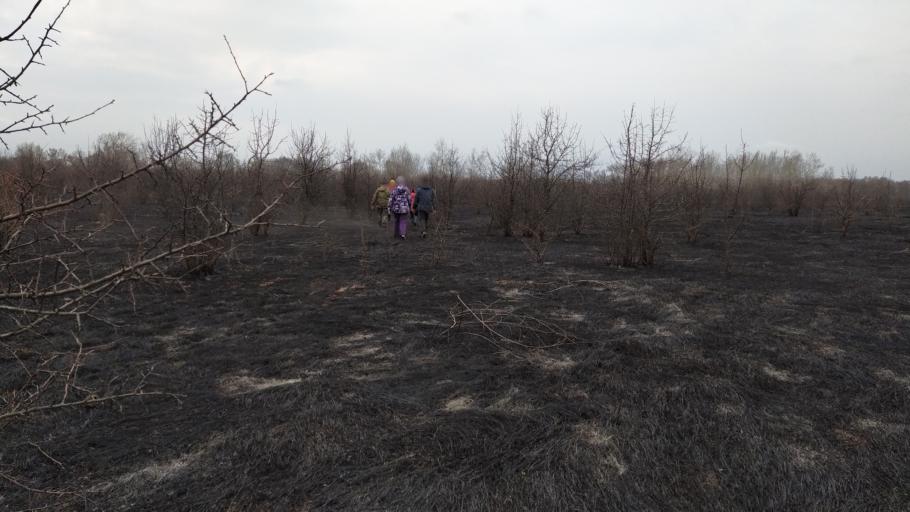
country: RU
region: Rostov
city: Semikarakorsk
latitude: 47.5425
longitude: 40.6840
